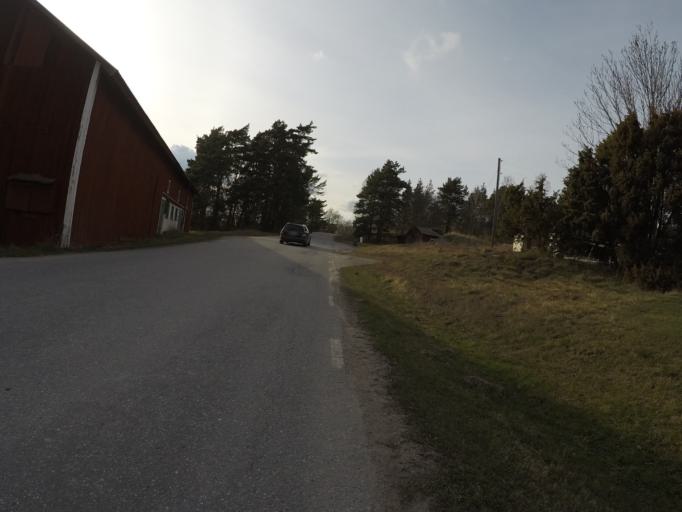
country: SE
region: Soedermanland
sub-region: Eskilstuna Kommun
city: Eskilstuna
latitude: 59.4338
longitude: 16.5568
